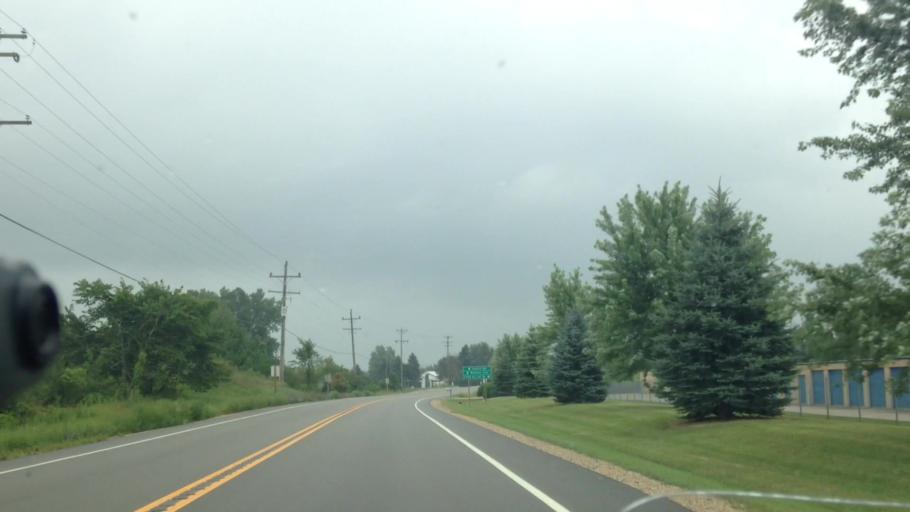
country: US
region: Wisconsin
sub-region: Washington County
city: Richfield
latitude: 43.2974
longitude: -88.2234
